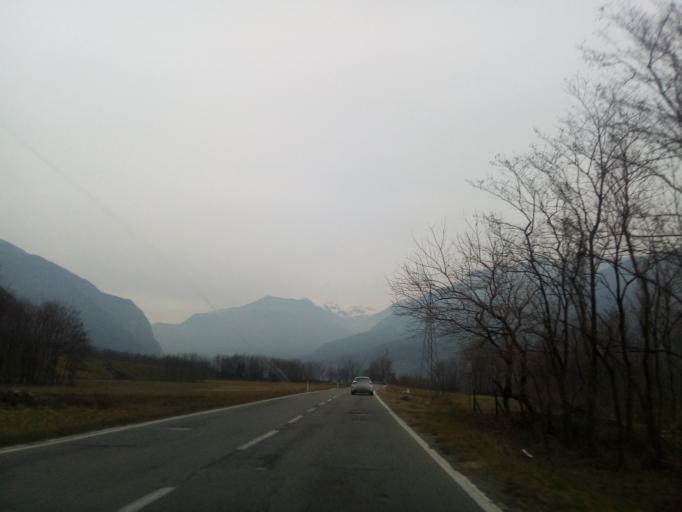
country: IT
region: Piedmont
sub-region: Provincia di Torino
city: Quassolo
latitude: 45.5334
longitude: 7.8319
